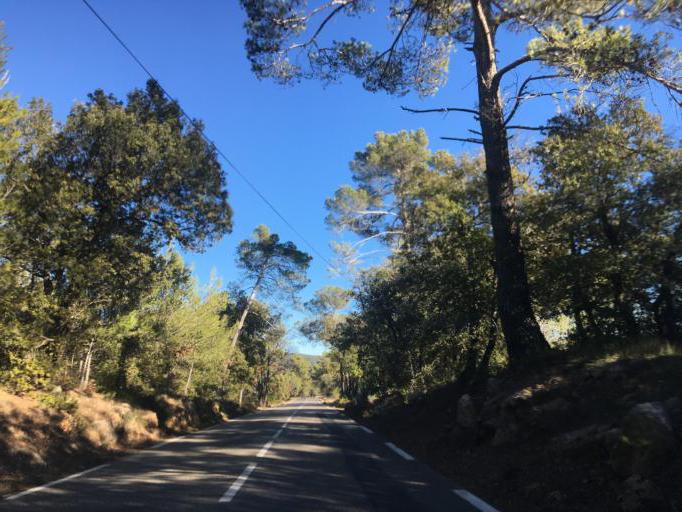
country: FR
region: Provence-Alpes-Cote d'Azur
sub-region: Departement du Var
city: Barjols
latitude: 43.5966
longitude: 5.9819
